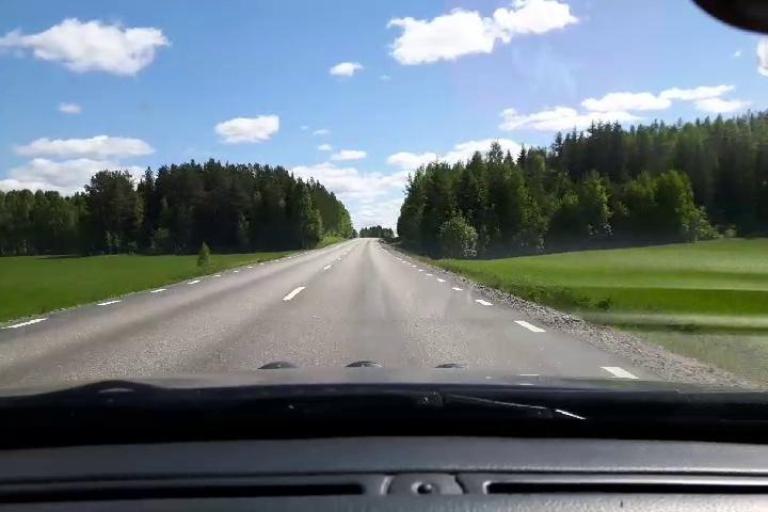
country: SE
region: Gaevleborg
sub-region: Ljusdals Kommun
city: Farila
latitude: 61.8739
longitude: 15.7230
